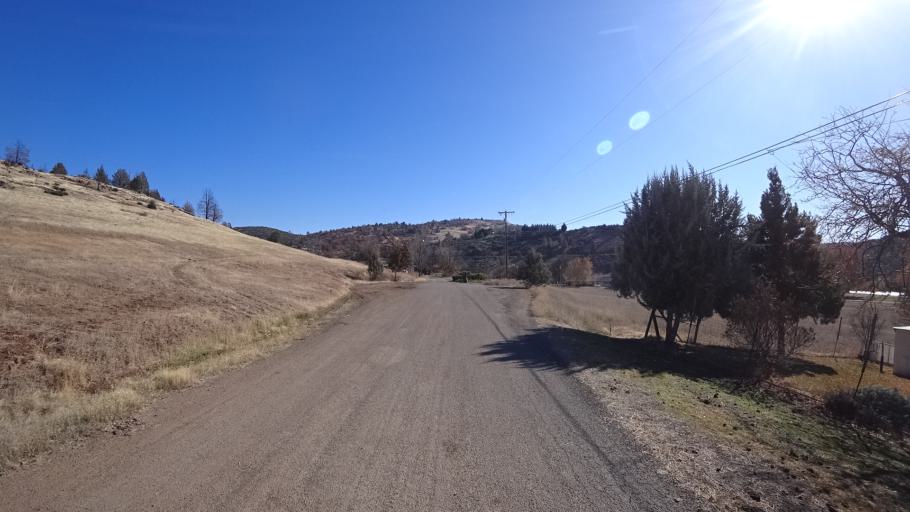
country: US
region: California
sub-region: Siskiyou County
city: Montague
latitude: 41.8976
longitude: -122.4847
